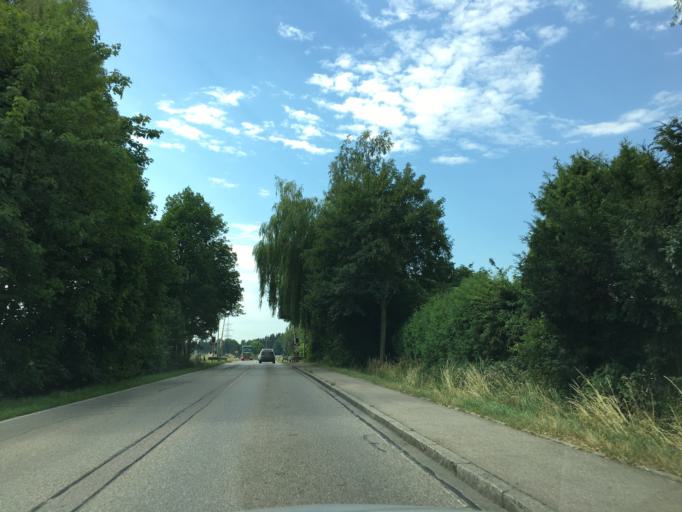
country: DE
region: Bavaria
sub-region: Upper Bavaria
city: Worth
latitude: 48.2401
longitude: 11.9374
